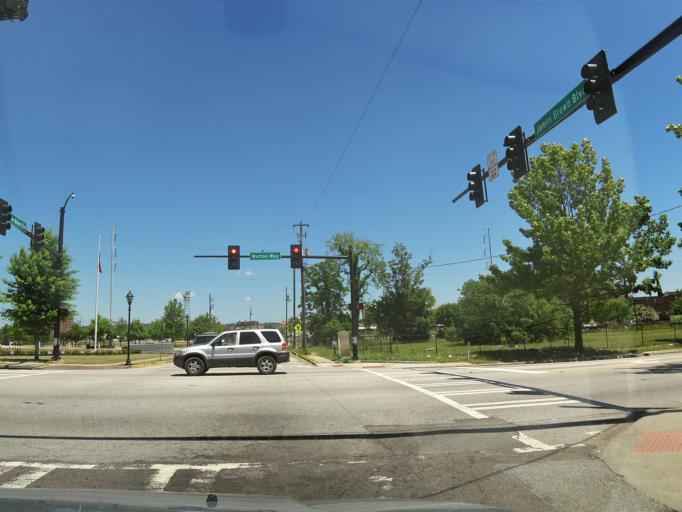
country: US
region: Georgia
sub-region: Richmond County
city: Augusta
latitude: 33.4689
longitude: -81.9712
